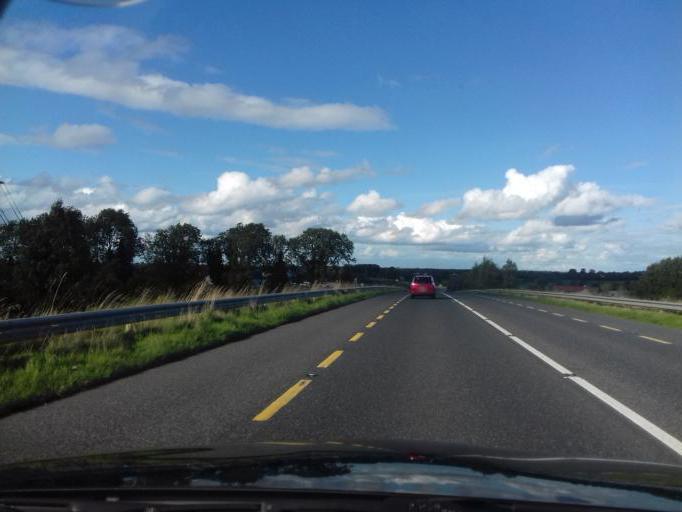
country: IE
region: Leinster
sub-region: Uibh Fhaili
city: Tullamore
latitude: 53.2618
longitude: -7.4654
